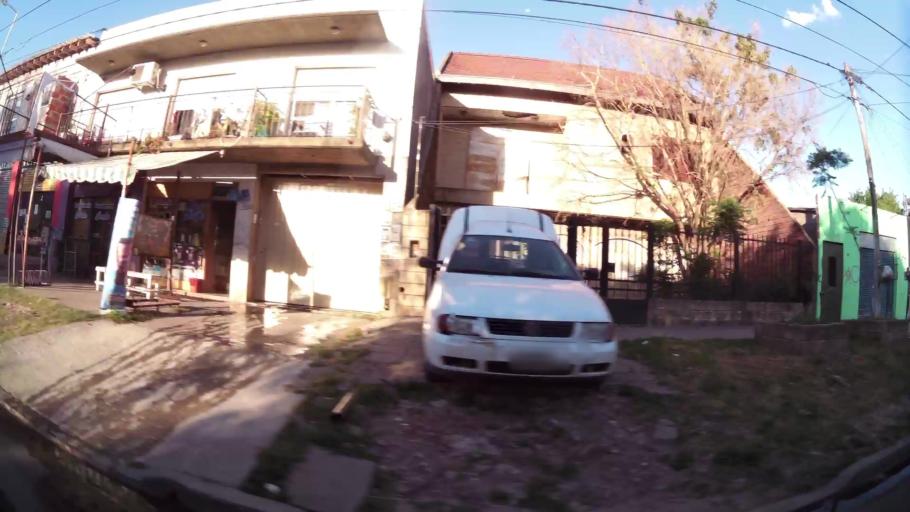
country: AR
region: Buenos Aires
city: Santa Catalina - Dique Lujan
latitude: -34.4708
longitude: -58.7526
